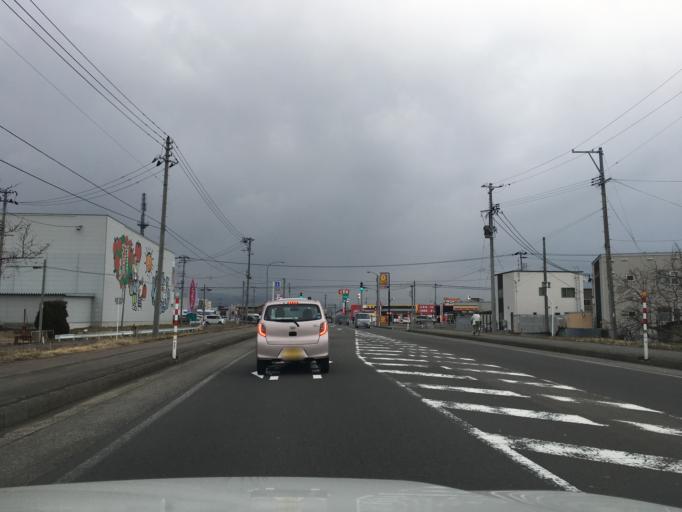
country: JP
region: Aomori
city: Kuroishi
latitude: 40.5871
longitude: 140.5689
